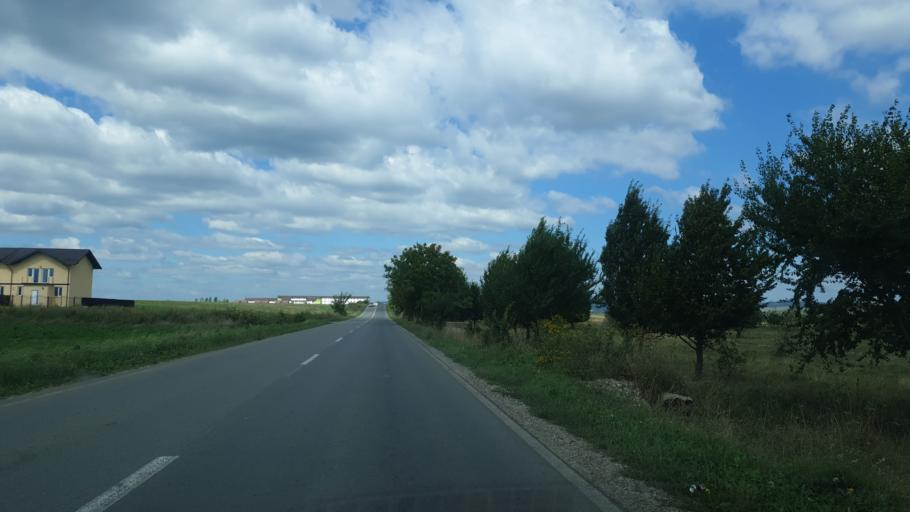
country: RO
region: Brasov
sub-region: Comuna Sanpetru
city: Sanpetru
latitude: 45.7217
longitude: 25.6277
